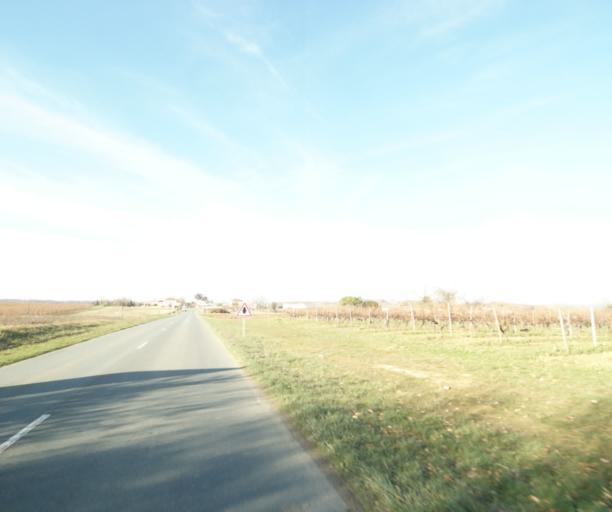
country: FR
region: Poitou-Charentes
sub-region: Departement de la Charente-Maritime
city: Burie
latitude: 45.7818
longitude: -0.4272
